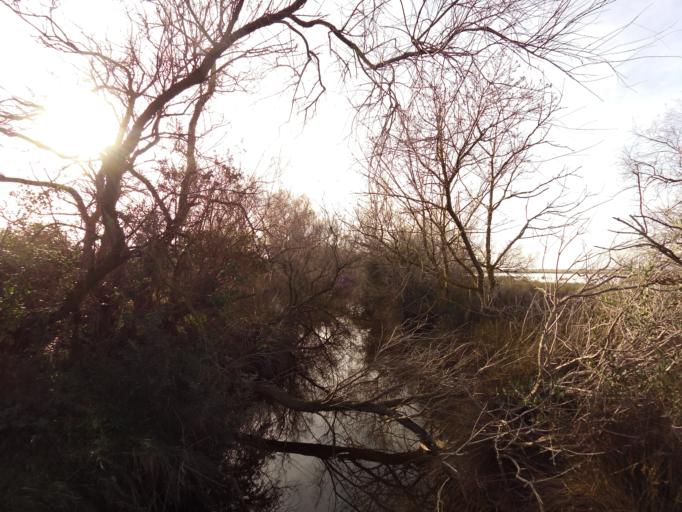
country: FR
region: Languedoc-Roussillon
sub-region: Departement du Gard
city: Aigues-Mortes
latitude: 43.5905
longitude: 4.2097
